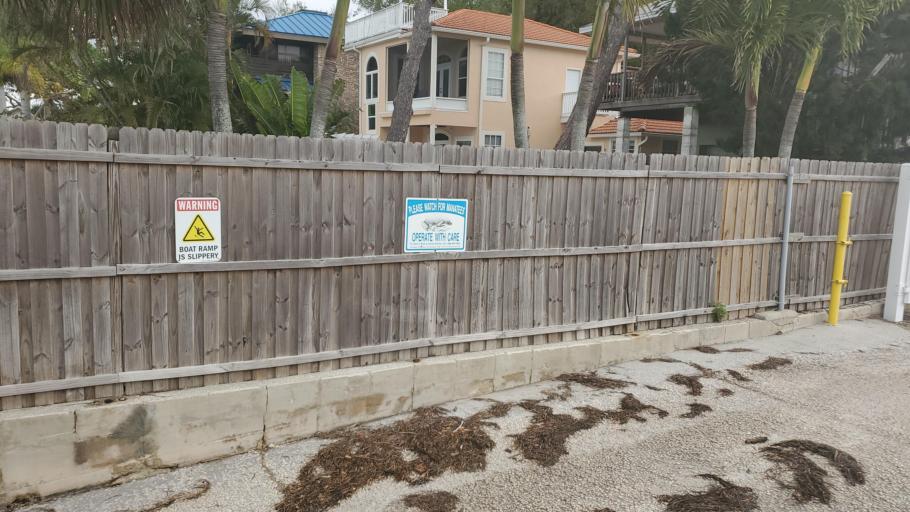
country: US
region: Florida
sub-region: Pinellas County
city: Palm Harbor
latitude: 28.0686
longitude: -82.7816
